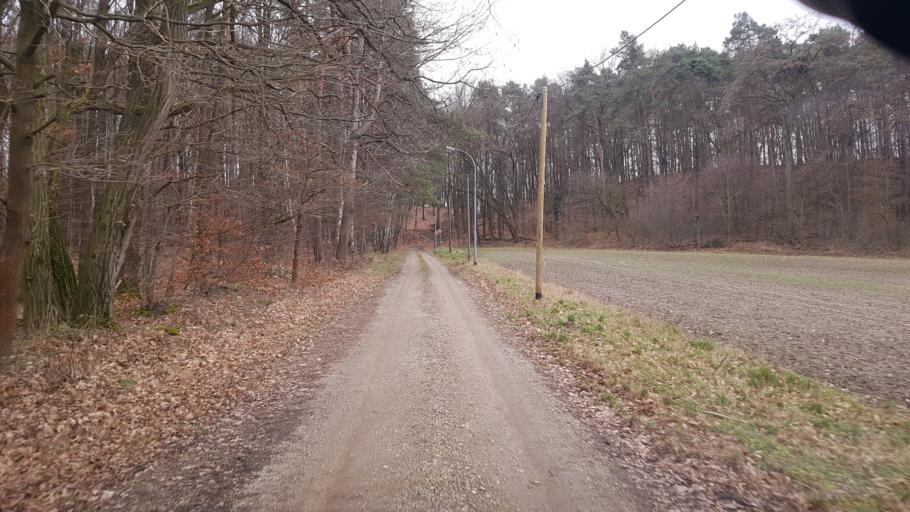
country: DE
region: Brandenburg
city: Crinitz
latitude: 51.7432
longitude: 13.7196
